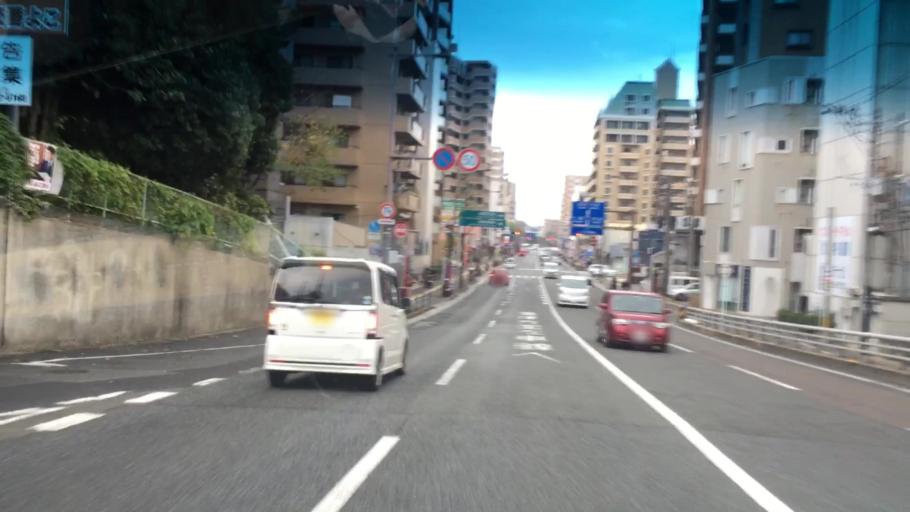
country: JP
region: Fukuoka
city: Fukuoka-shi
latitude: 33.5752
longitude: 130.3721
